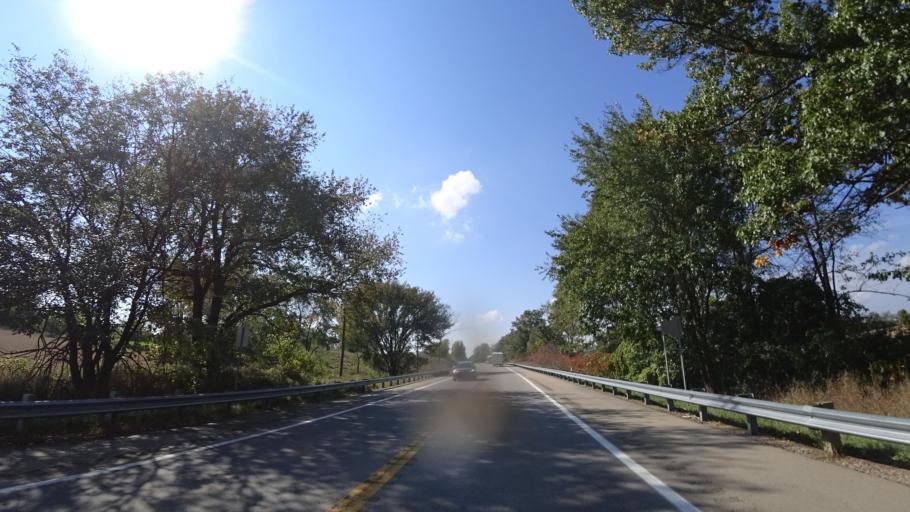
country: US
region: Michigan
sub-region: Jackson County
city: Concord
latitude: 42.1919
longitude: -84.6137
